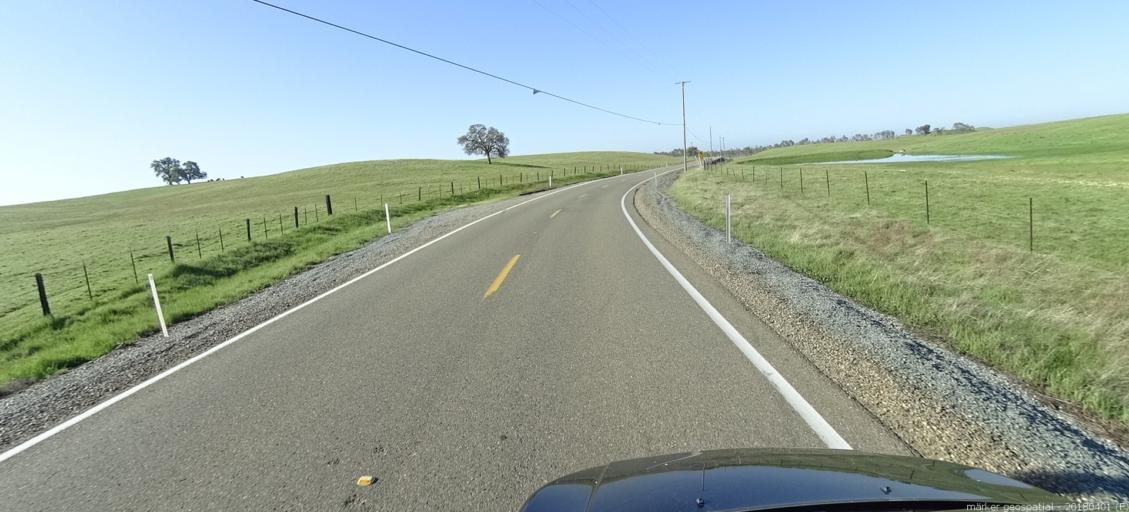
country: US
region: California
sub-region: Sacramento County
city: Rancho Murieta
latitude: 38.4476
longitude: -121.0470
